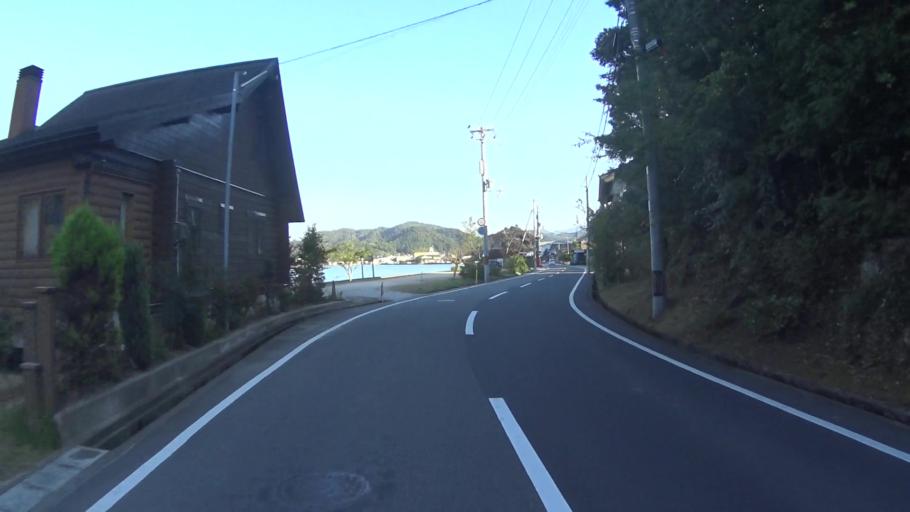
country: JP
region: Hyogo
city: Toyooka
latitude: 35.6104
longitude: 134.8893
